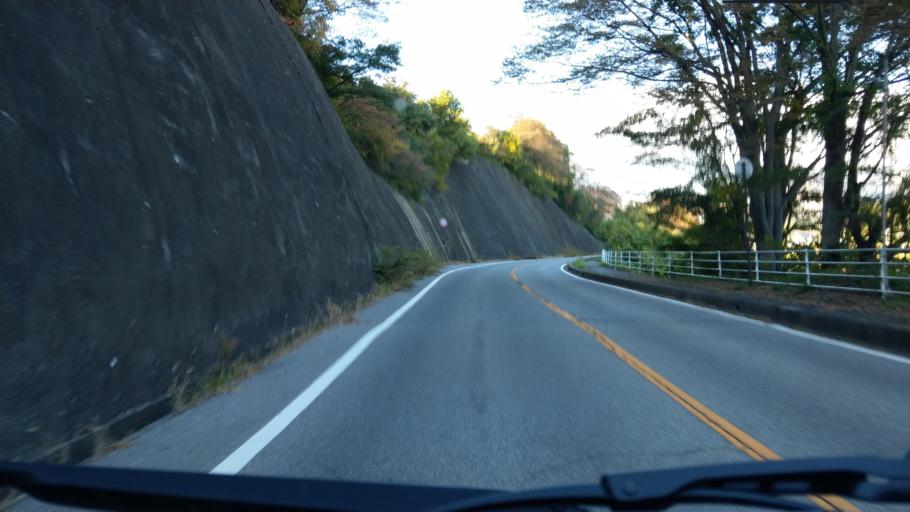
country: JP
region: Nagano
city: Komoro
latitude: 36.3468
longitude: 138.4294
